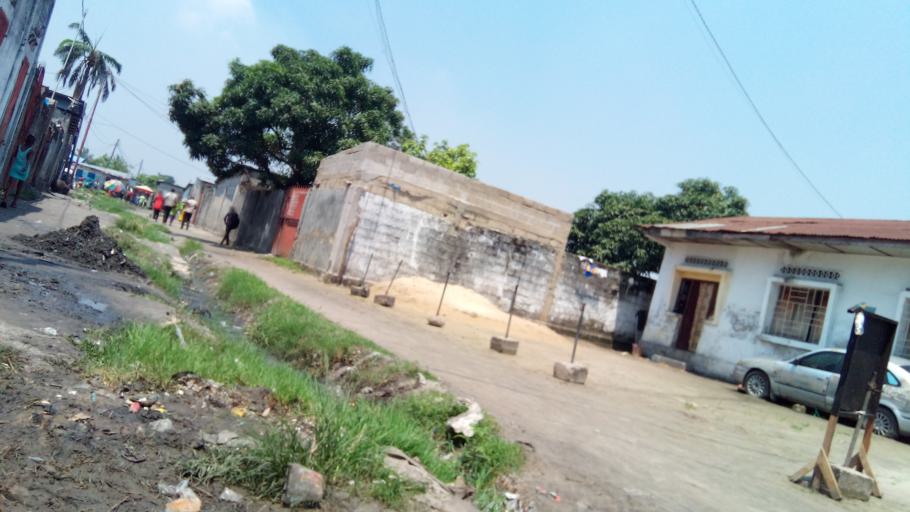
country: CD
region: Kinshasa
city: Kinshasa
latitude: -4.3682
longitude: 15.3094
